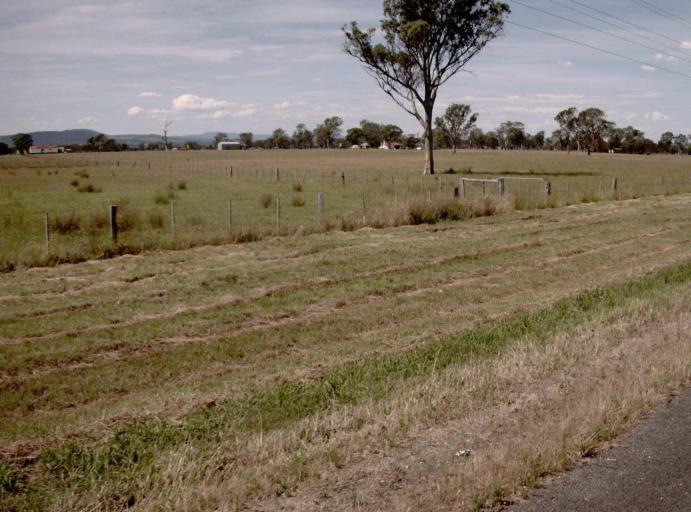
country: AU
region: Victoria
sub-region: East Gippsland
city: Bairnsdale
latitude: -37.8625
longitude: 147.5064
